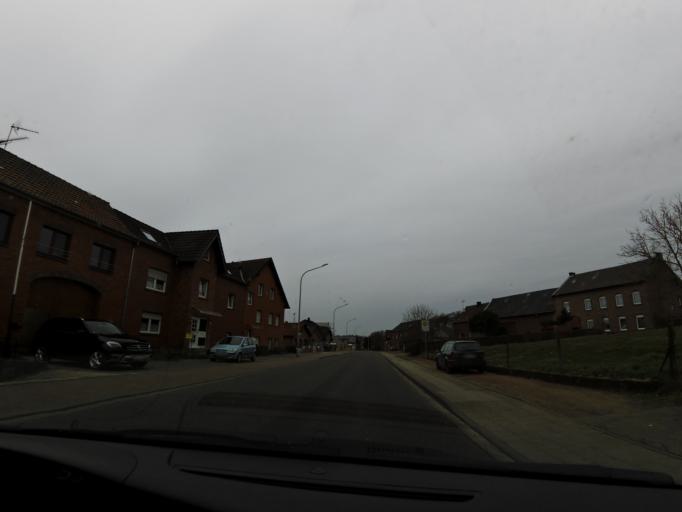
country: DE
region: North Rhine-Westphalia
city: Geilenkirchen
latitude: 50.9696
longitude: 6.0775
